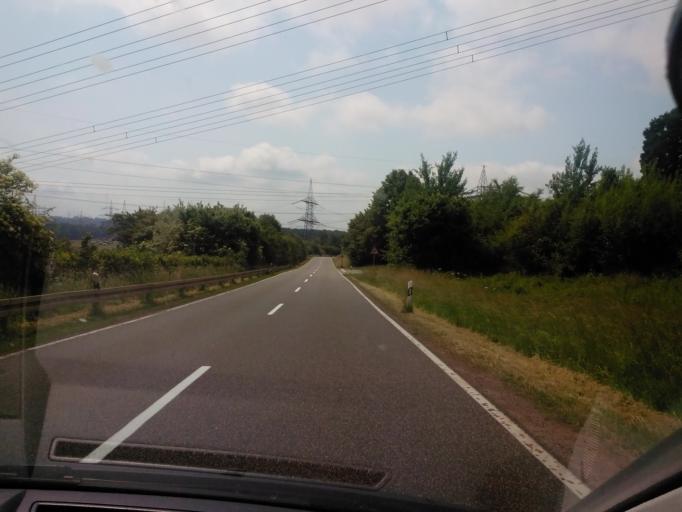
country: DE
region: Saarland
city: Eppelborn
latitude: 49.3775
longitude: 7.0000
